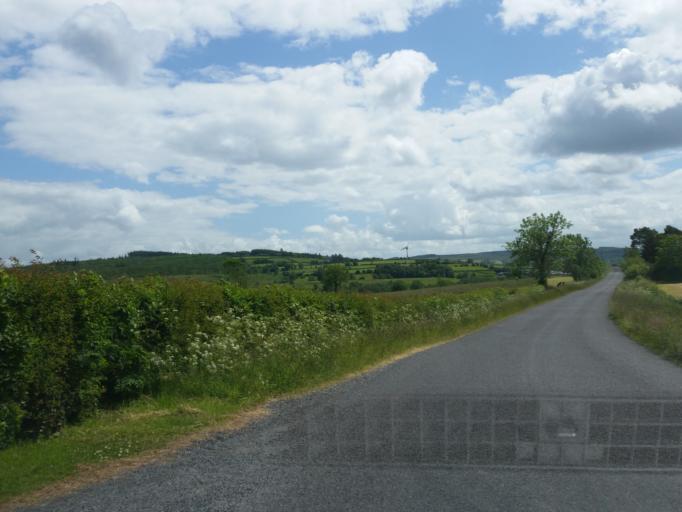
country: GB
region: Northern Ireland
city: Fivemiletown
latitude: 54.3524
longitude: -7.2983
